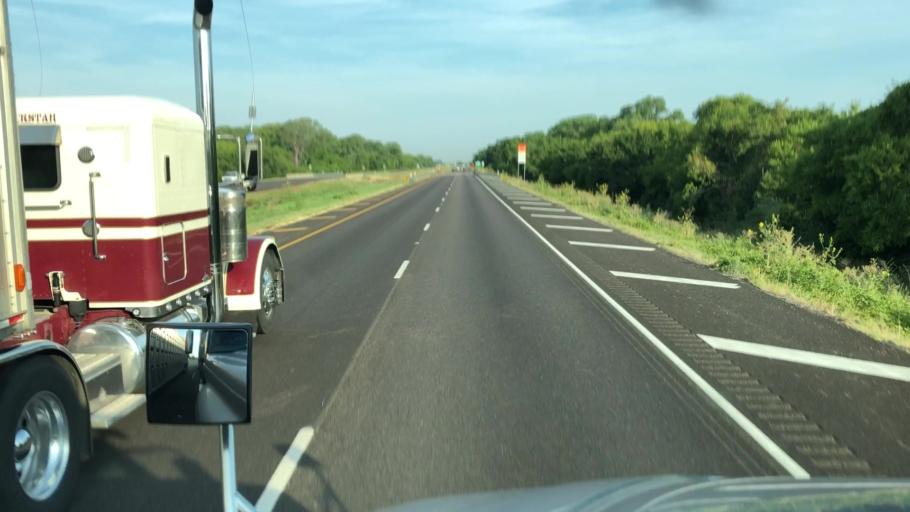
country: US
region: Texas
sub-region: McLennan County
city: Bellmead
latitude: 31.5397
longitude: -97.0438
